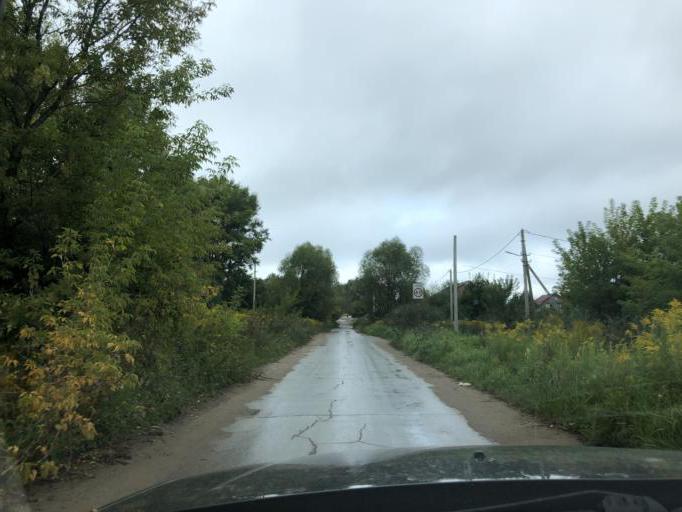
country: RU
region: Tula
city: Mendeleyevskiy
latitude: 54.1730
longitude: 37.5526
